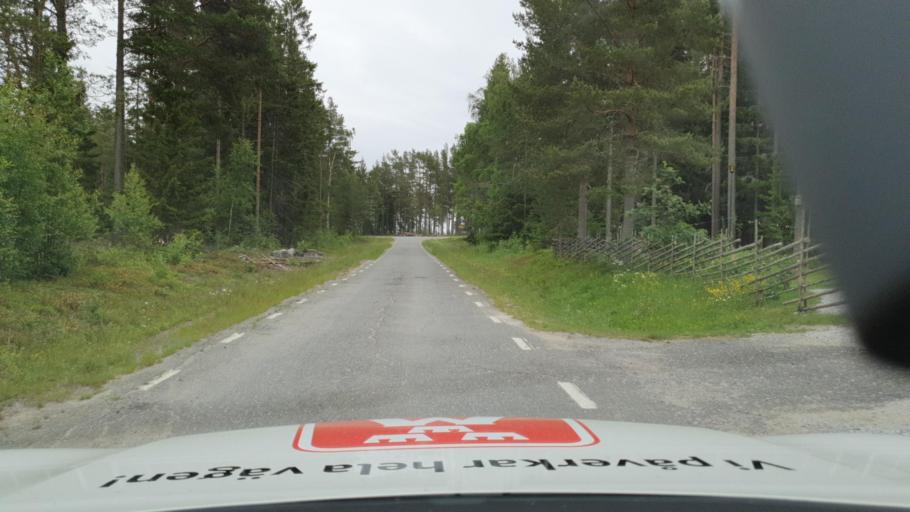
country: SE
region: Vaesterbotten
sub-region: Nordmalings Kommun
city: Nordmaling
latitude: 63.4245
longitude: 19.4991
